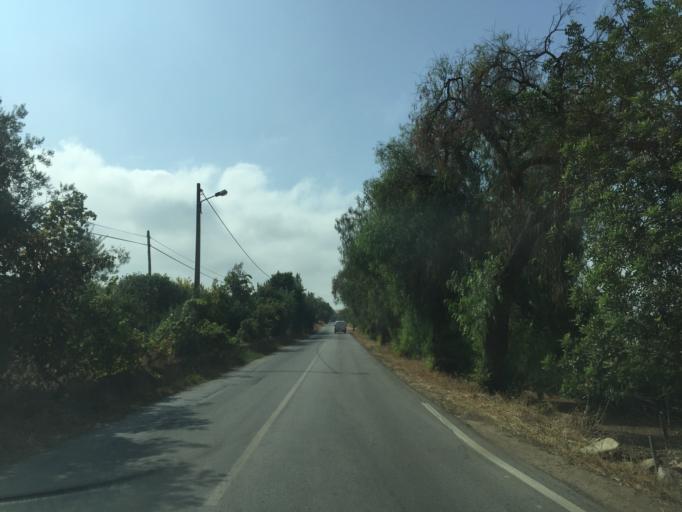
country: PT
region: Faro
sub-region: Sao Bras de Alportel
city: Sao Bras de Alportel
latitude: 37.0851
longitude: -7.8919
